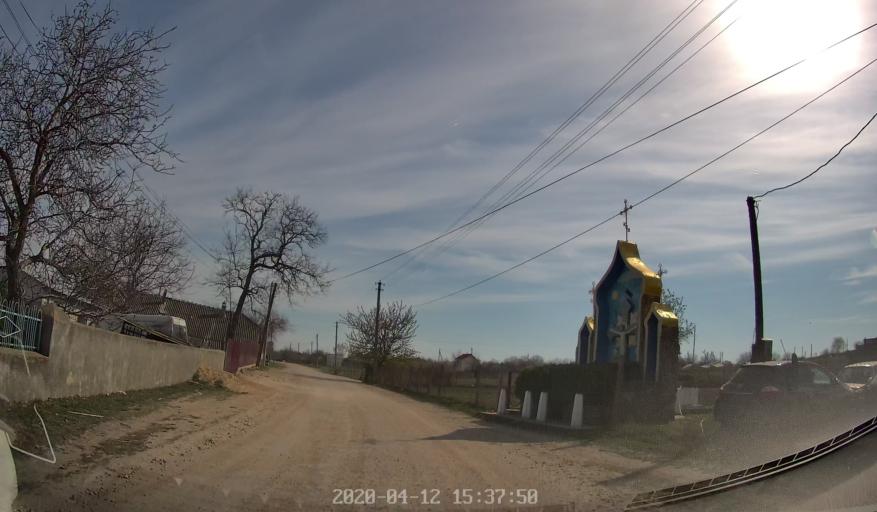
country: MD
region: Telenesti
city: Cocieri
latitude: 47.3210
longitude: 29.0684
